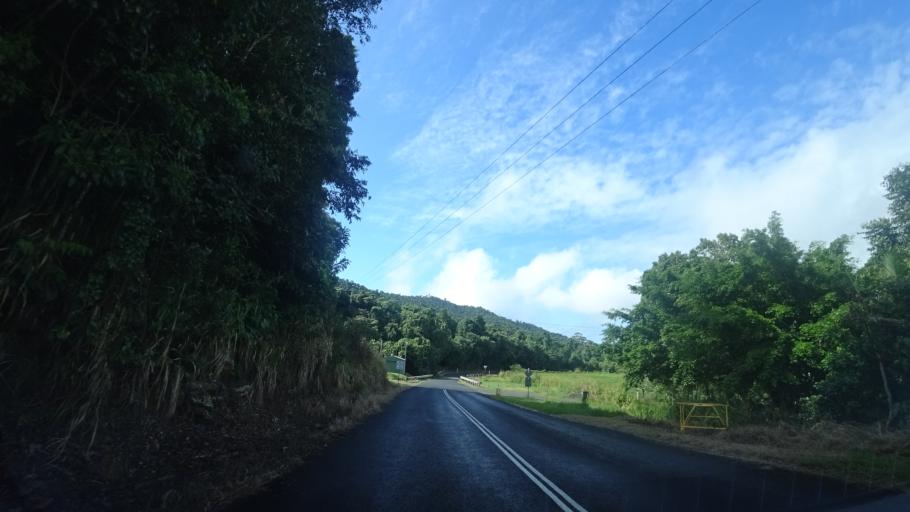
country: AU
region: Queensland
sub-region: Cassowary Coast
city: Innisfail
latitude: -17.5664
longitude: 146.0859
